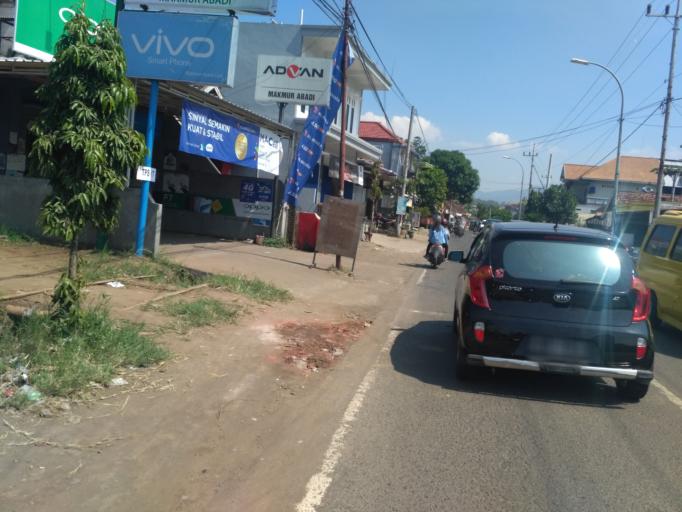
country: ID
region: East Java
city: Batu
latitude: -7.8640
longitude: 112.5562
